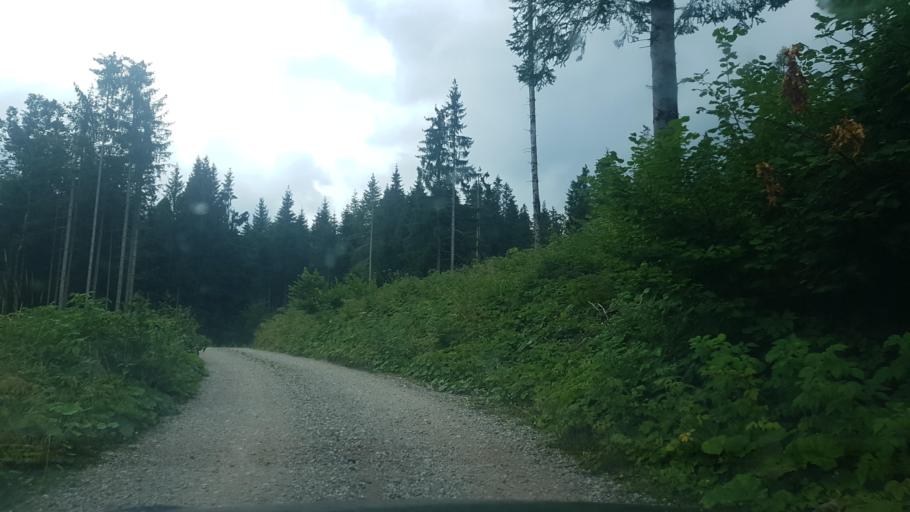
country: IT
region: Friuli Venezia Giulia
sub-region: Provincia di Udine
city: Rigolato
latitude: 46.5591
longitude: 12.8133
